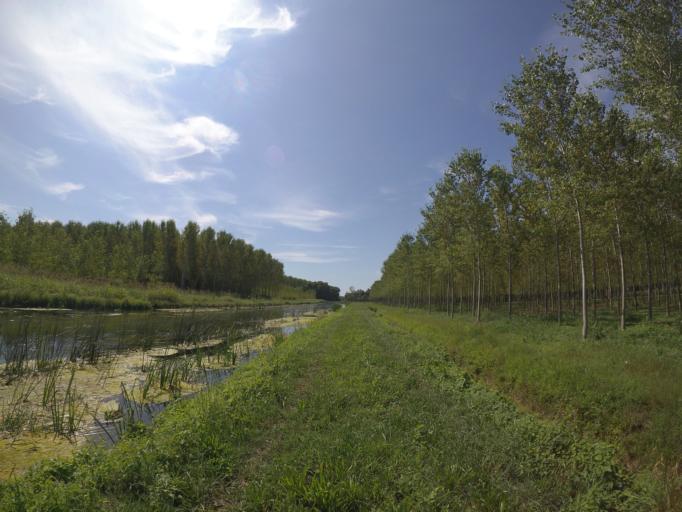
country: IT
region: Friuli Venezia Giulia
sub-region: Provincia di Udine
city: Bertiolo
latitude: 45.9178
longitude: 13.0216
